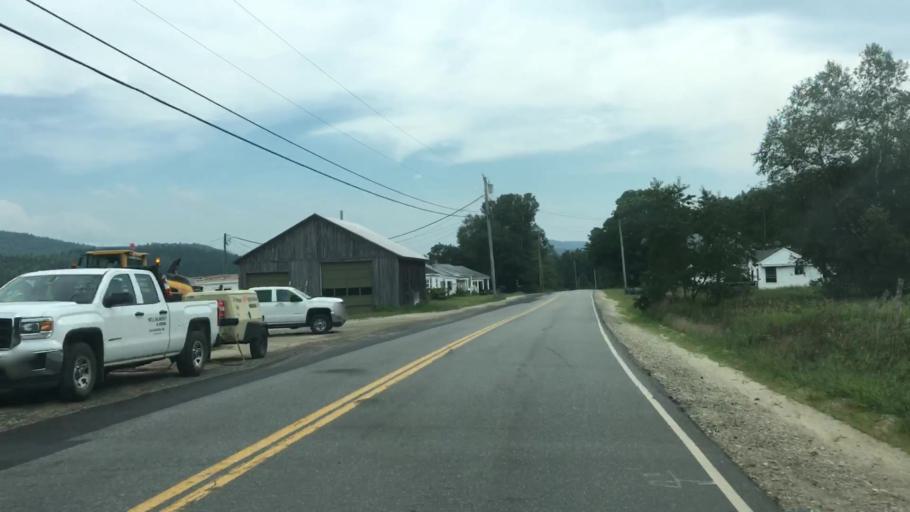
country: US
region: Maine
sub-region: Oxford County
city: Rumford
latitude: 44.5341
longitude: -70.6830
